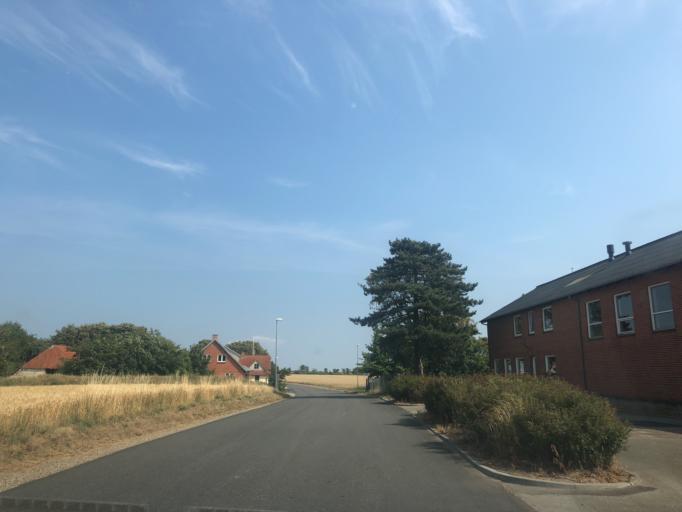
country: DK
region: North Denmark
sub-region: Morso Kommune
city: Nykobing Mors
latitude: 56.8172
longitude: 9.0131
